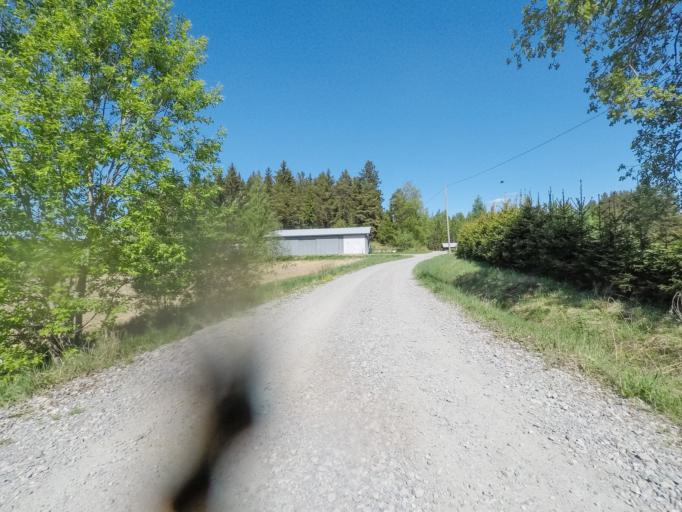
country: FI
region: Pirkanmaa
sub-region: Etelae-Pirkanmaa
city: Kylmaekoski
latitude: 61.1612
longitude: 23.7097
